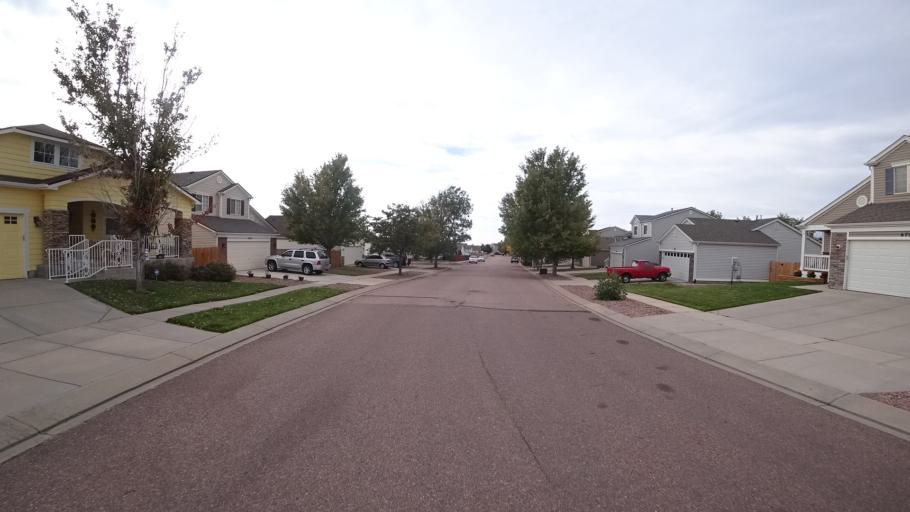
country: US
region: Colorado
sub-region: El Paso County
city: Cimarron Hills
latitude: 38.9178
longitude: -104.7057
